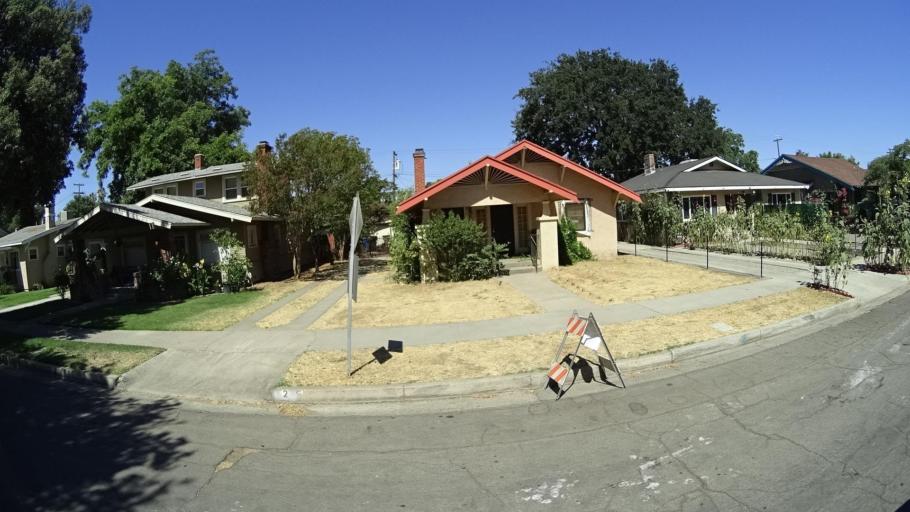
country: US
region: California
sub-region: Fresno County
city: Fresno
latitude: 36.7590
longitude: -119.8046
